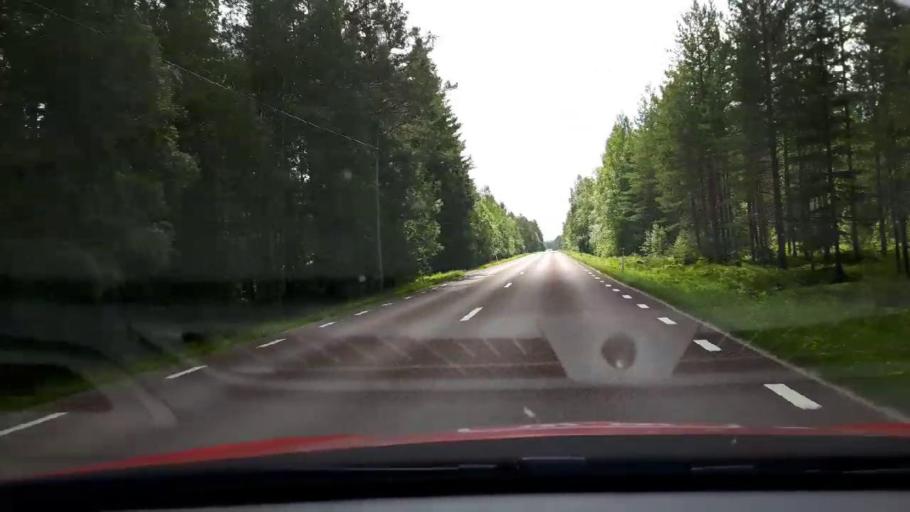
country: SE
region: Jaemtland
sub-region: Harjedalens Kommun
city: Sveg
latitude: 62.1166
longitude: 14.9701
